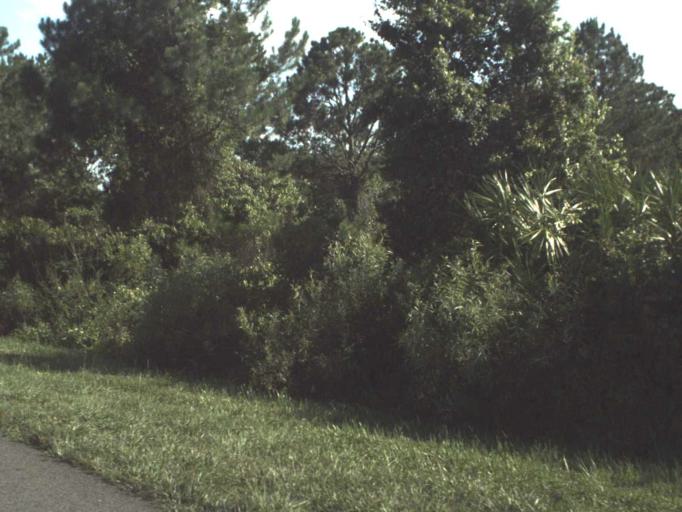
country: US
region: Florida
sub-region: Lake County
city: Clermont
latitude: 28.3914
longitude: -81.8257
